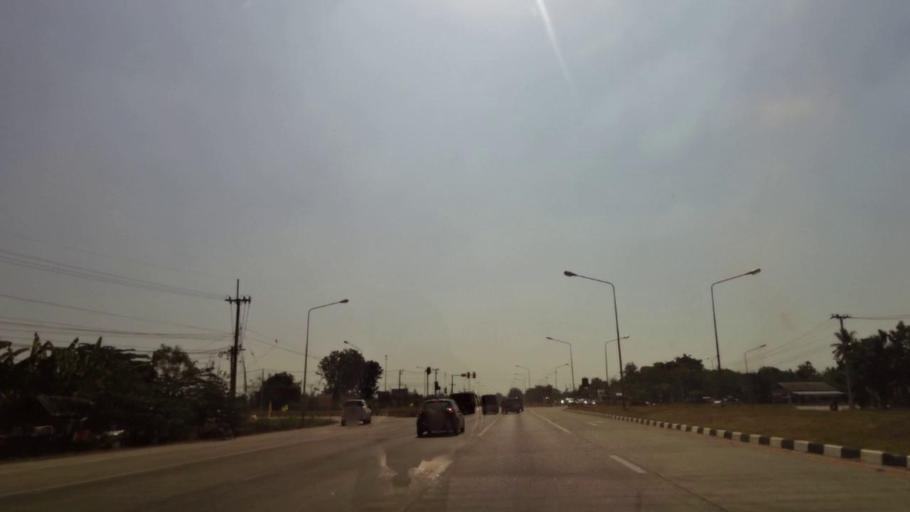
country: TH
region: Phichit
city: Wachira Barami
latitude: 16.3557
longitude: 100.1293
